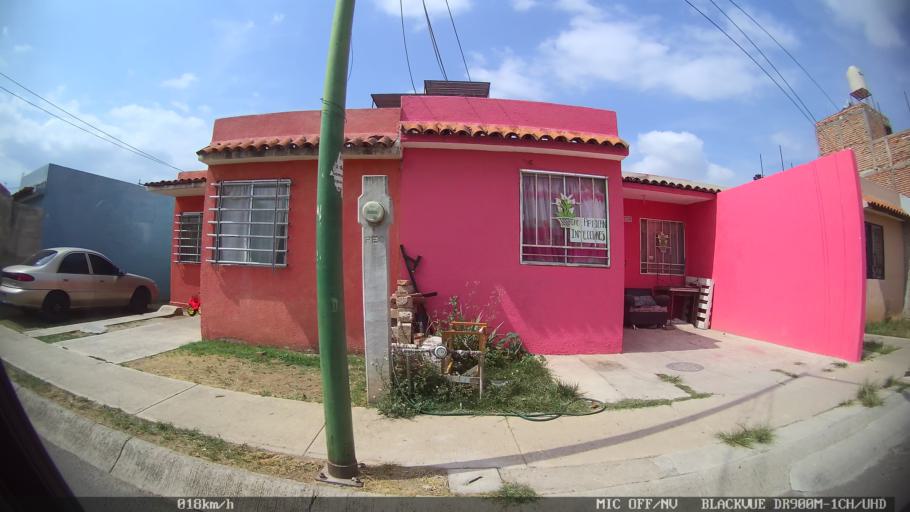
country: MX
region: Jalisco
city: Coyula
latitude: 20.6406
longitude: -103.2174
